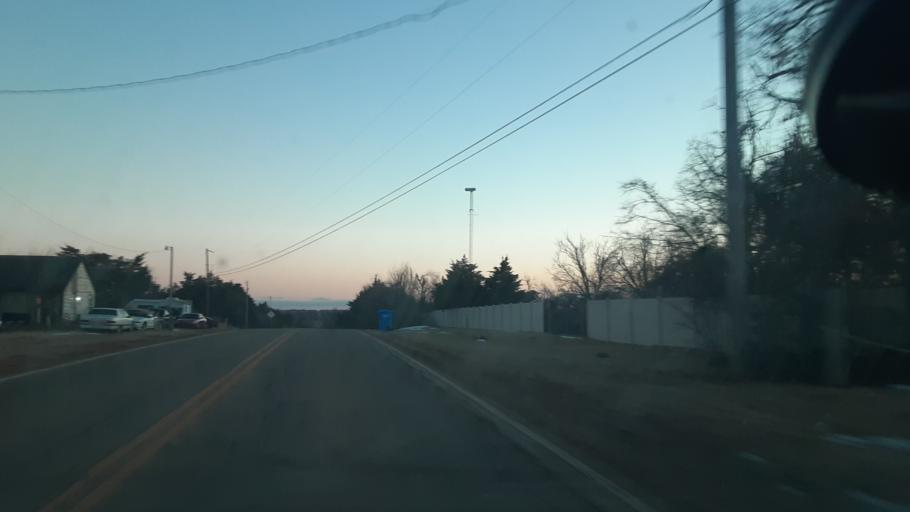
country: US
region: Oklahoma
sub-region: Oklahoma County
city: Edmond
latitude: 35.7243
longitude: -97.4252
